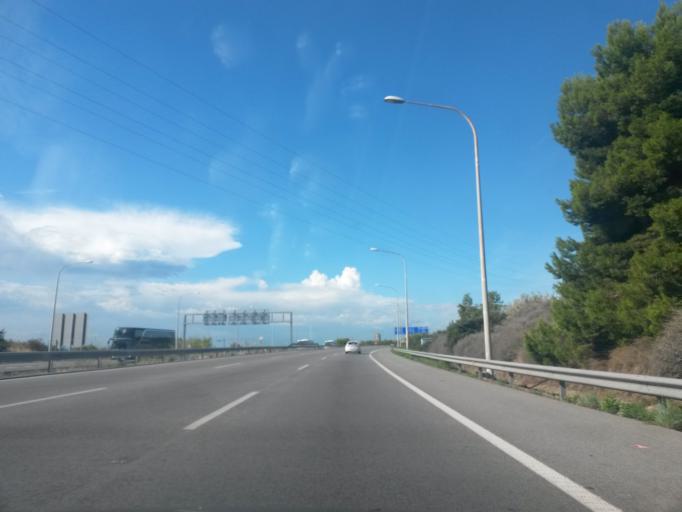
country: ES
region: Catalonia
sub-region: Provincia de Barcelona
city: Alella
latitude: 41.4824
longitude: 2.2941
